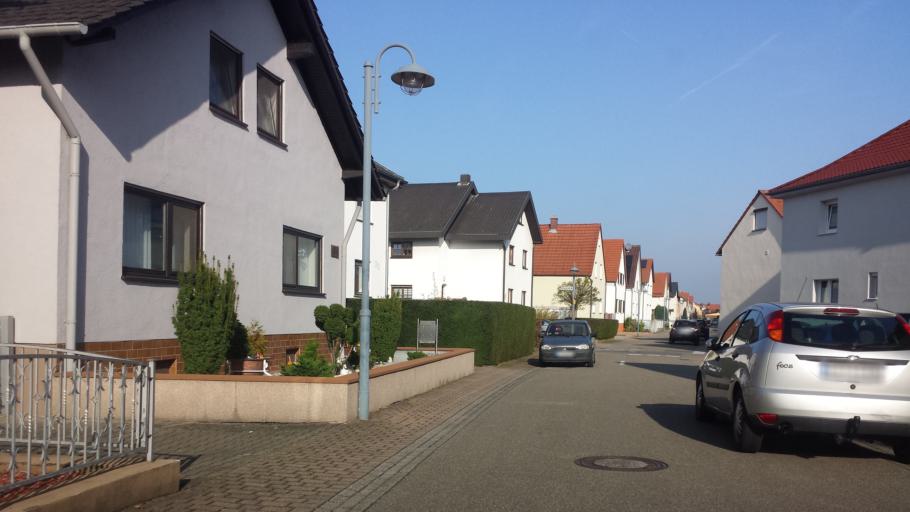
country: DE
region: Baden-Wuerttemberg
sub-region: Karlsruhe Region
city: Kronau
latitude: 49.2160
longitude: 8.6300
